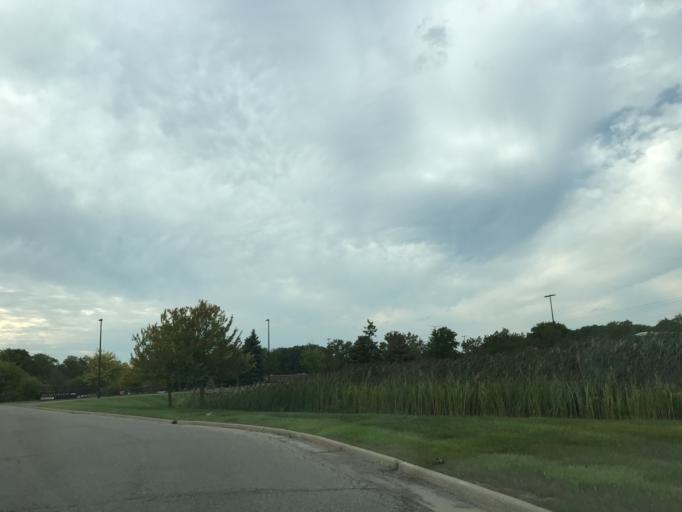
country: US
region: Michigan
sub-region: Oakland County
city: Novi
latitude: 42.4834
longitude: -83.4569
